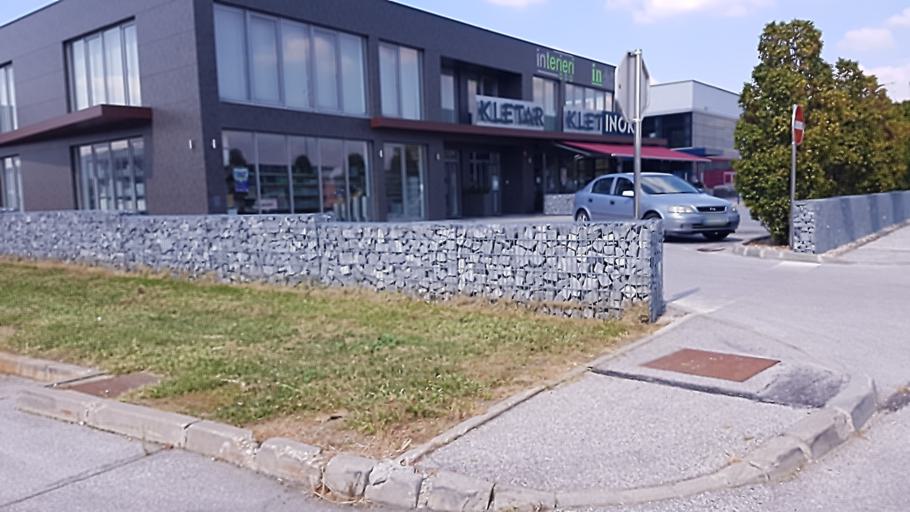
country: SI
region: Ljutomer
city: Ljutomer
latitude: 46.5302
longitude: 16.1881
